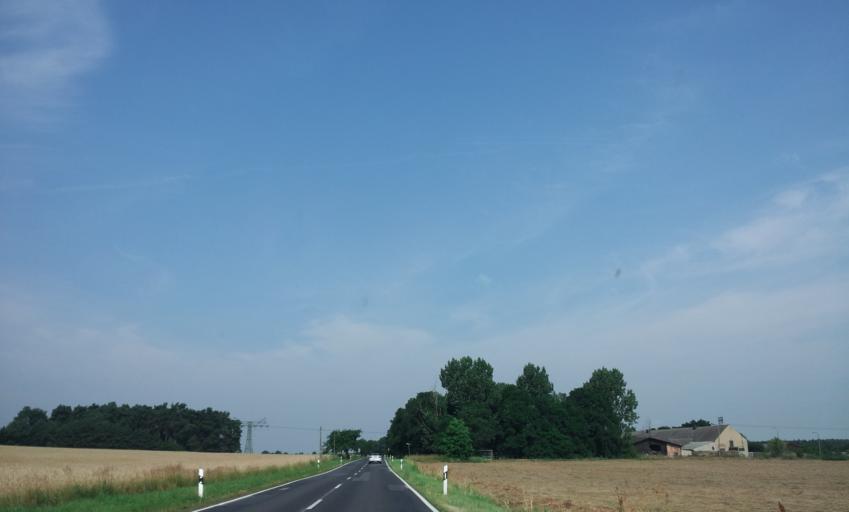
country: DE
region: Brandenburg
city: Treuenbrietzen
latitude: 52.0985
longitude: 12.8496
